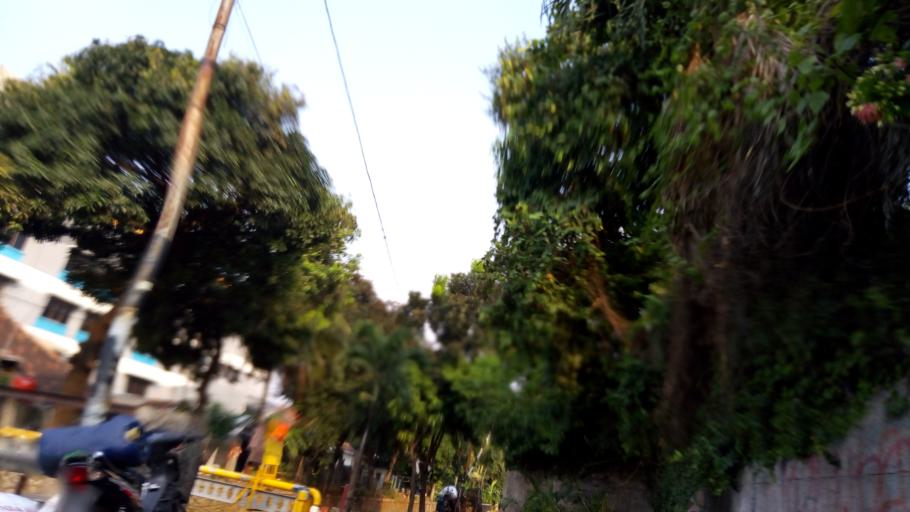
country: ID
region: Jakarta Raya
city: Jakarta
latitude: -6.1936
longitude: 106.8509
